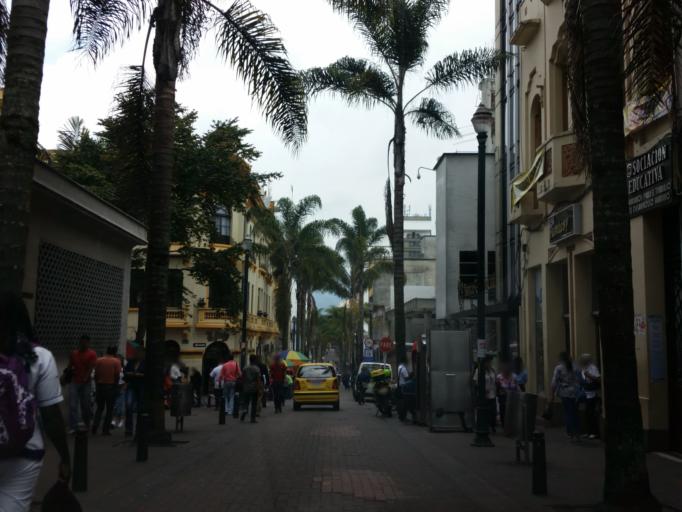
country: CO
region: Caldas
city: Manizales
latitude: 5.0671
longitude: -75.5173
